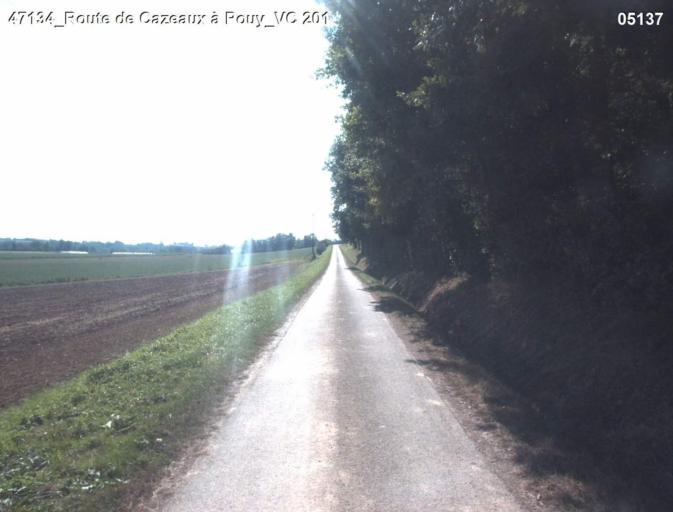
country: FR
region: Aquitaine
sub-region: Departement du Lot-et-Garonne
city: Mezin
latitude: 44.0413
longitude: 0.3109
